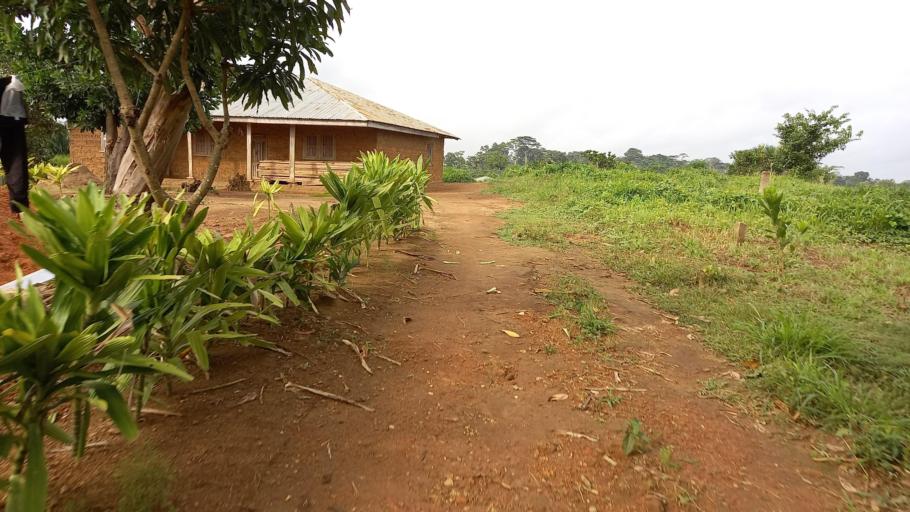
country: SL
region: Eastern Province
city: Kailahun
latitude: 8.2729
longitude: -10.5827
